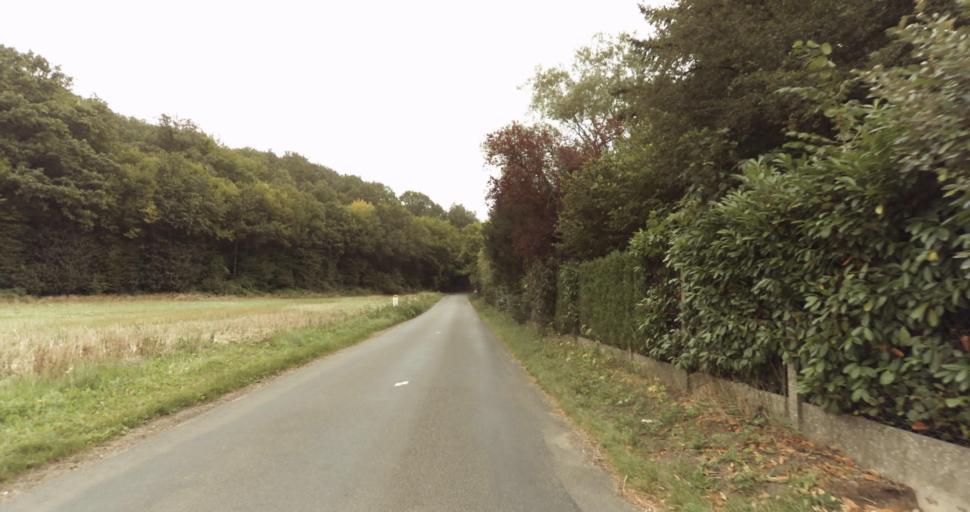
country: FR
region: Haute-Normandie
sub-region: Departement de l'Eure
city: La Couture-Boussey
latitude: 48.8924
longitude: 1.3887
